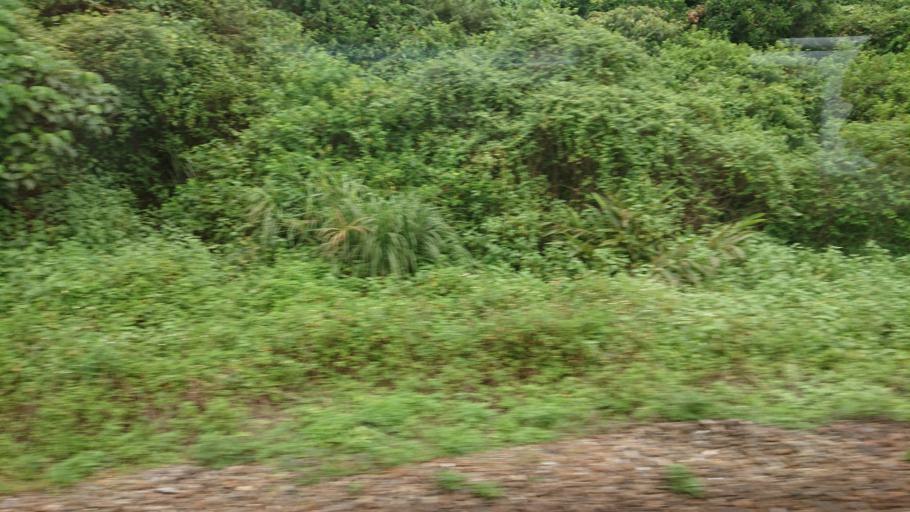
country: TW
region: Taiwan
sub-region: Yilan
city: Yilan
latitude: 24.9118
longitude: 121.8767
